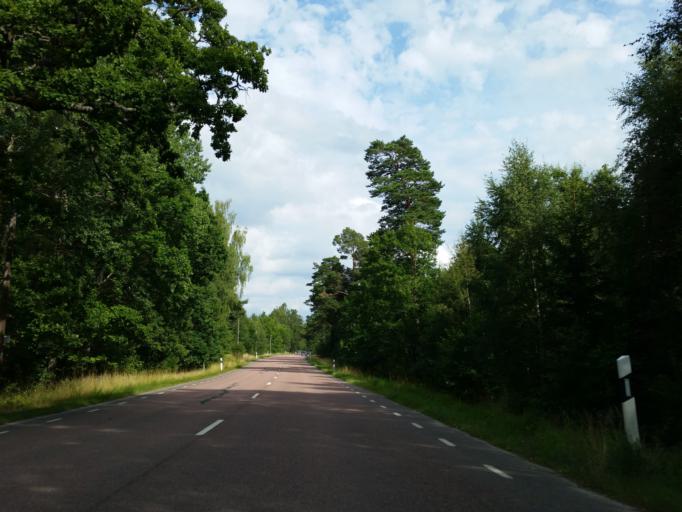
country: SE
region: Soedermanland
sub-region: Strangnas Kommun
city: Mariefred
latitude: 59.2216
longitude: 17.2711
